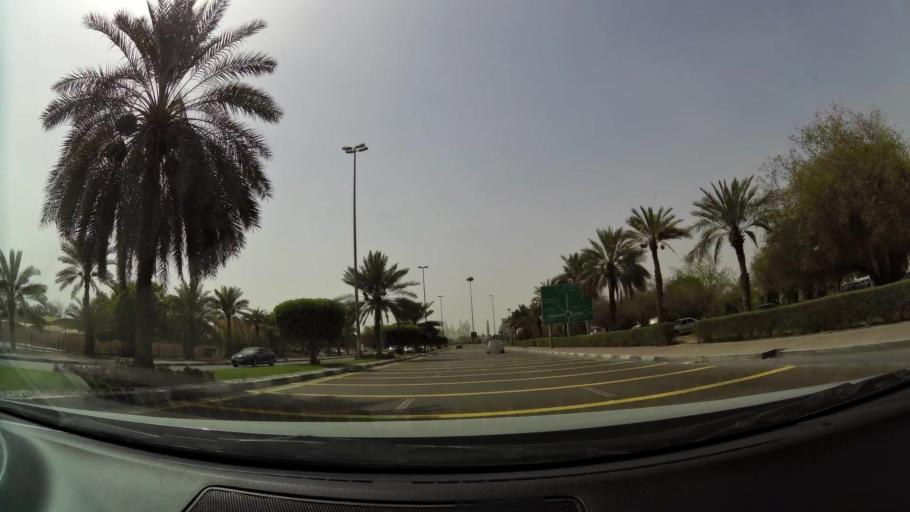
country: AE
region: Abu Dhabi
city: Al Ain
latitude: 24.1924
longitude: 55.6559
